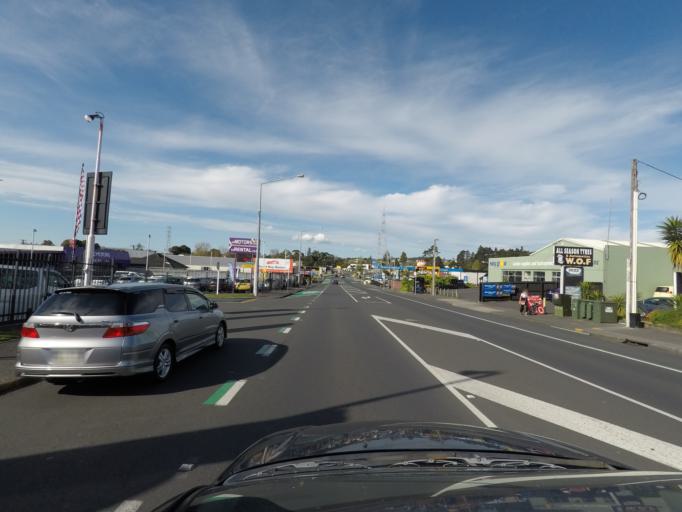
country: NZ
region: Auckland
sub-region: Auckland
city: Waitakere
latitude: -36.9046
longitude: 174.6873
